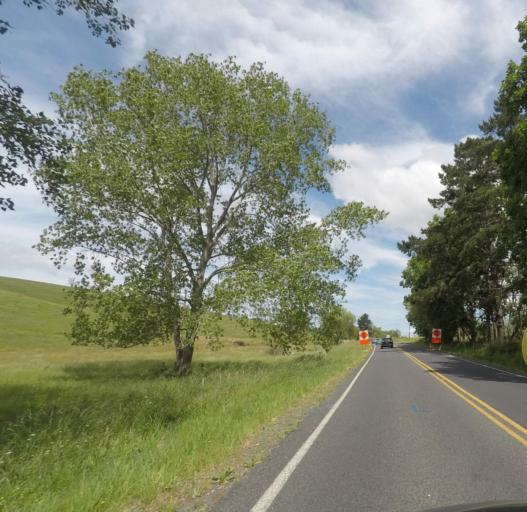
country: NZ
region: Auckland
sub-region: Auckland
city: Rothesay Bay
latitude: -36.6671
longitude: 174.6793
